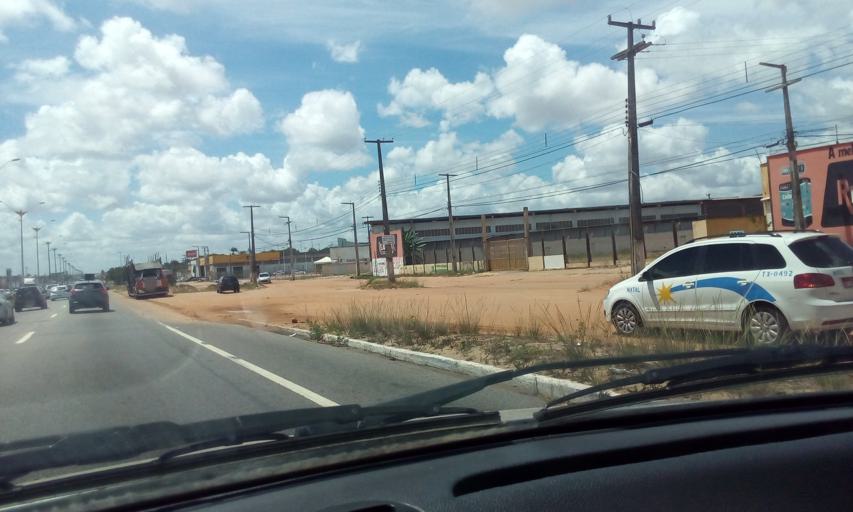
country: BR
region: Rio Grande do Norte
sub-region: Parnamirim
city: Parnamirim
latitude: -5.8988
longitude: -35.2588
